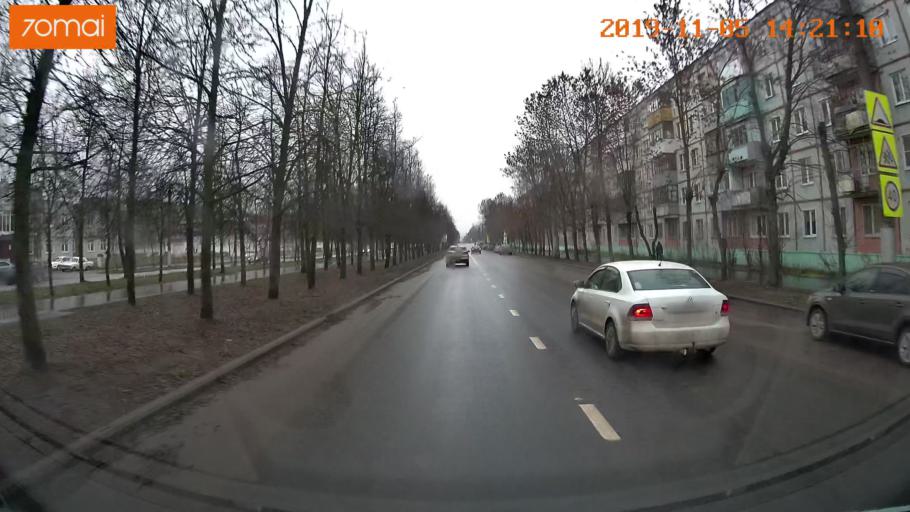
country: RU
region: Ivanovo
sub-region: Gorod Ivanovo
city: Ivanovo
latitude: 56.9575
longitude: 41.0132
